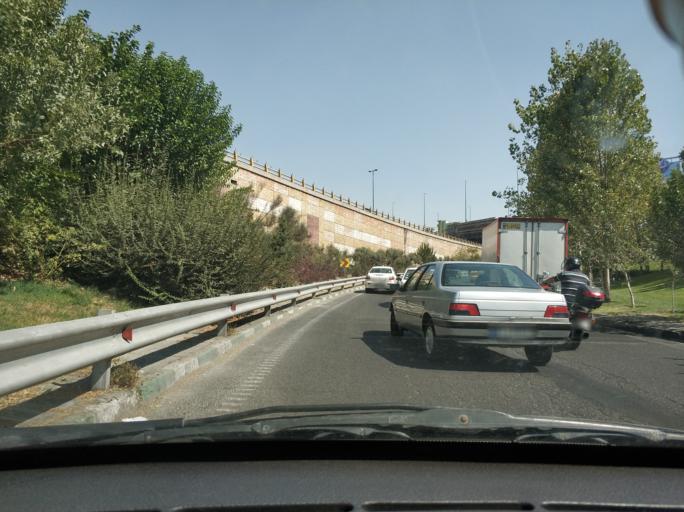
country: IR
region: Tehran
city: Tehran
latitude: 35.7429
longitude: 51.3853
